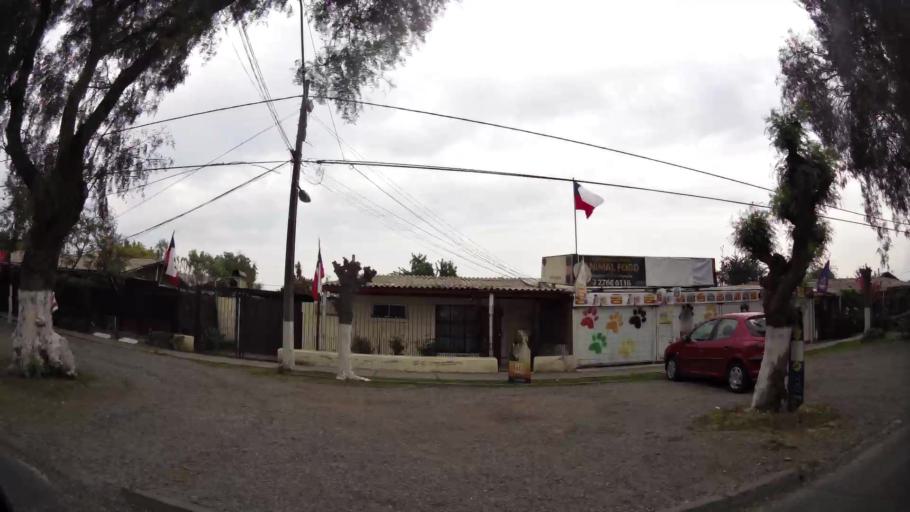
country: CL
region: Santiago Metropolitan
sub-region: Provincia de Santiago
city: Lo Prado
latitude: -33.4994
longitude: -70.7692
